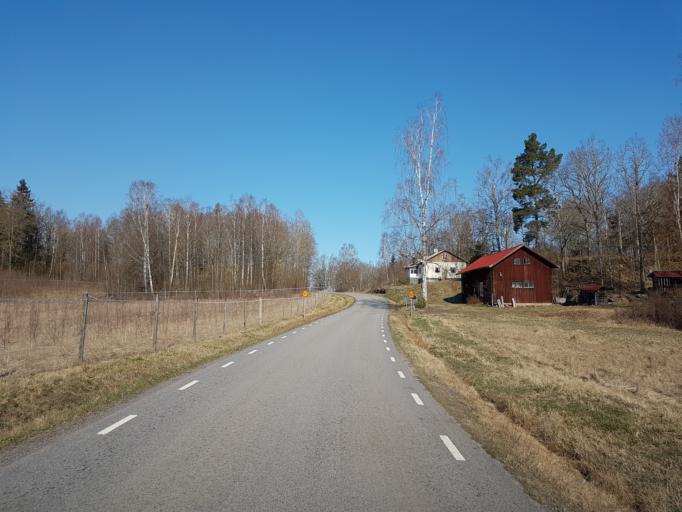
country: SE
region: OEstergoetland
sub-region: Valdemarsviks Kommun
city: Gusum
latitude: 58.1906
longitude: 16.2939
